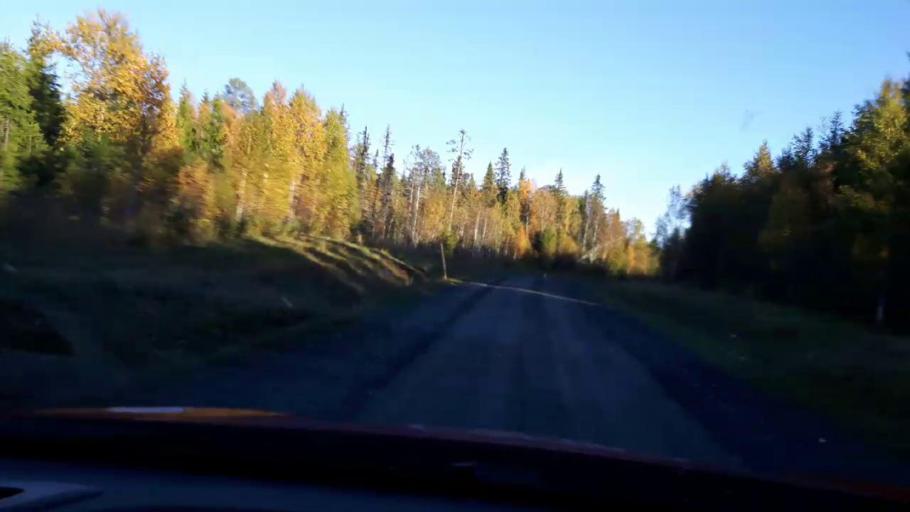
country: SE
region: Jaemtland
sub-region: OEstersunds Kommun
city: Lit
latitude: 63.5945
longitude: 14.8344
